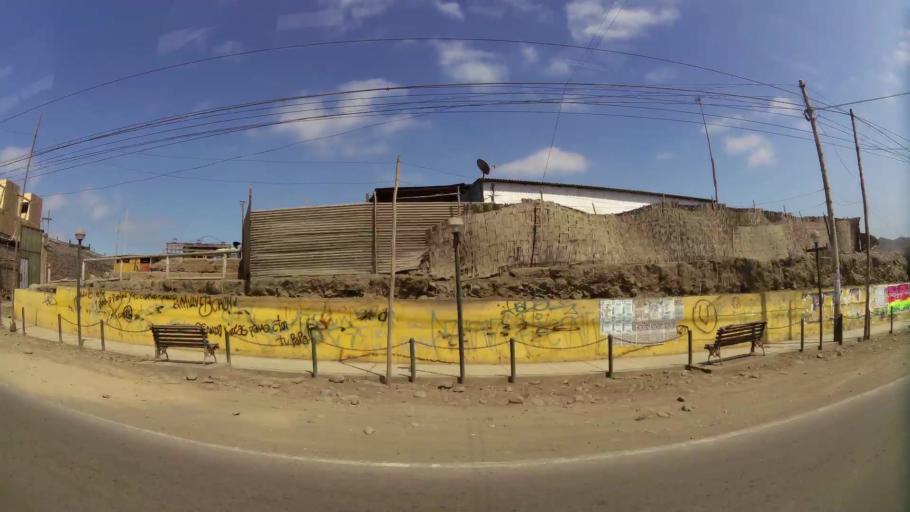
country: PE
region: Lima
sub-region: Provincia de Canete
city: Mala
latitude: -12.6549
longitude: -76.6371
